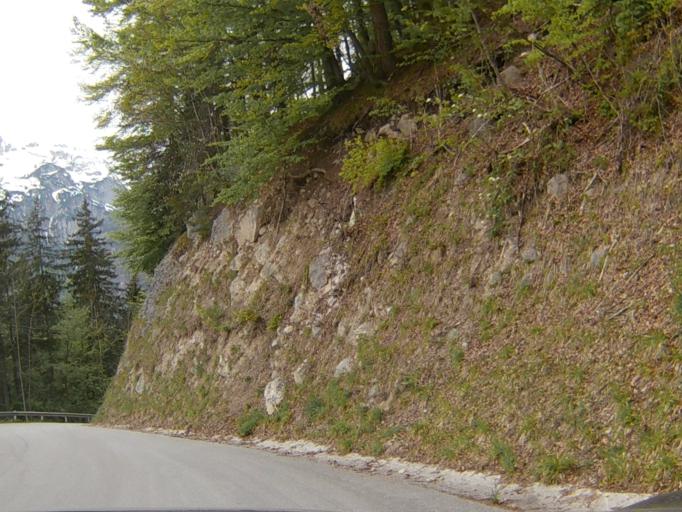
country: AT
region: Salzburg
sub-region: Politischer Bezirk Sankt Johann im Pongau
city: Werfen
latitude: 47.4865
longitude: 13.1979
